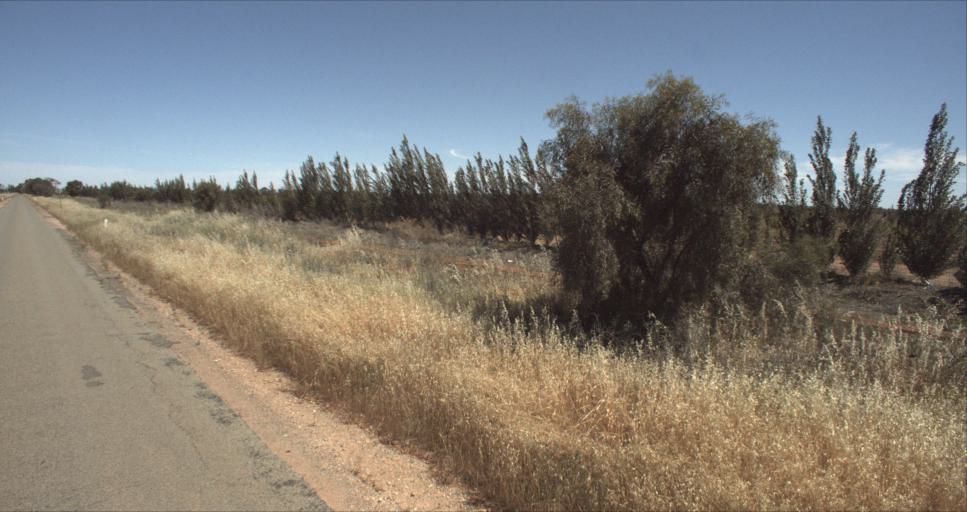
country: AU
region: New South Wales
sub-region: Leeton
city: Leeton
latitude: -34.5126
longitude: 146.3450
